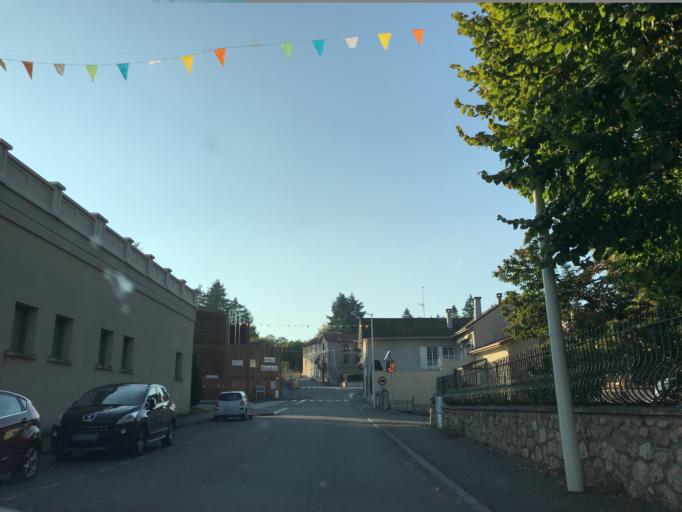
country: FR
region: Rhone-Alpes
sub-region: Departement de la Loire
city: Noiretable
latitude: 45.8173
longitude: 3.7643
